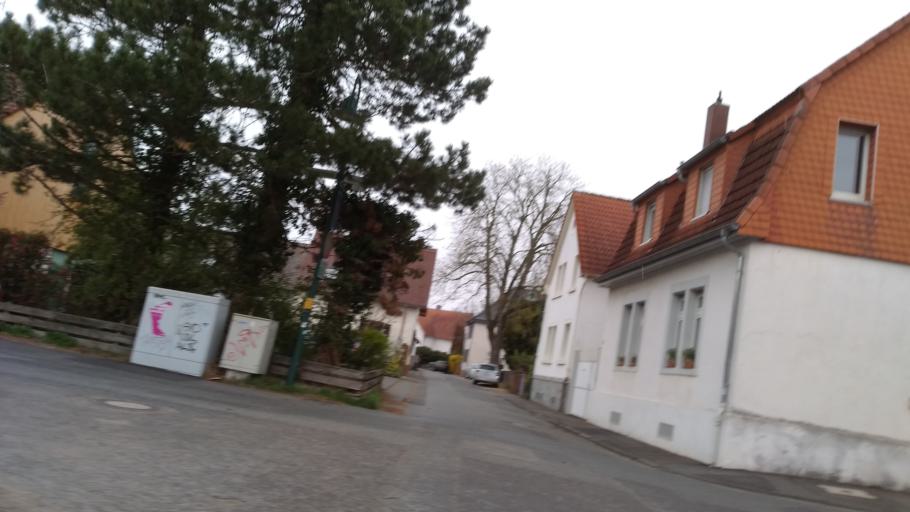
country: DE
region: Hesse
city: Pfungstadt
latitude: 49.8137
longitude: 8.6422
